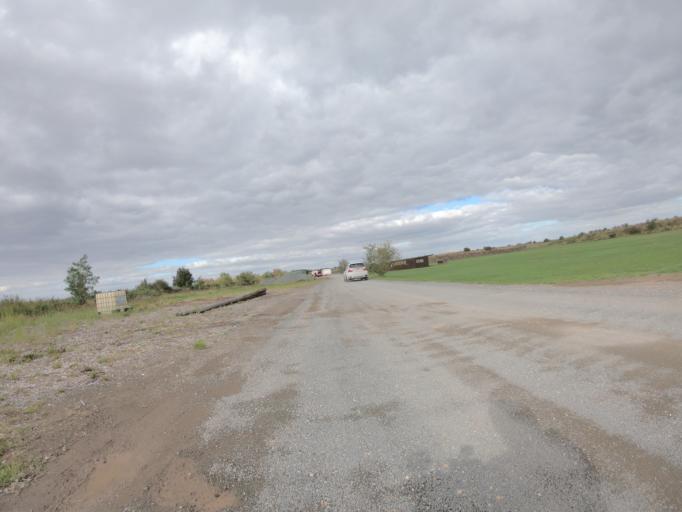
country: GB
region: England
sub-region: Essex
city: Purfleet
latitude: 51.4728
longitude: 0.2216
